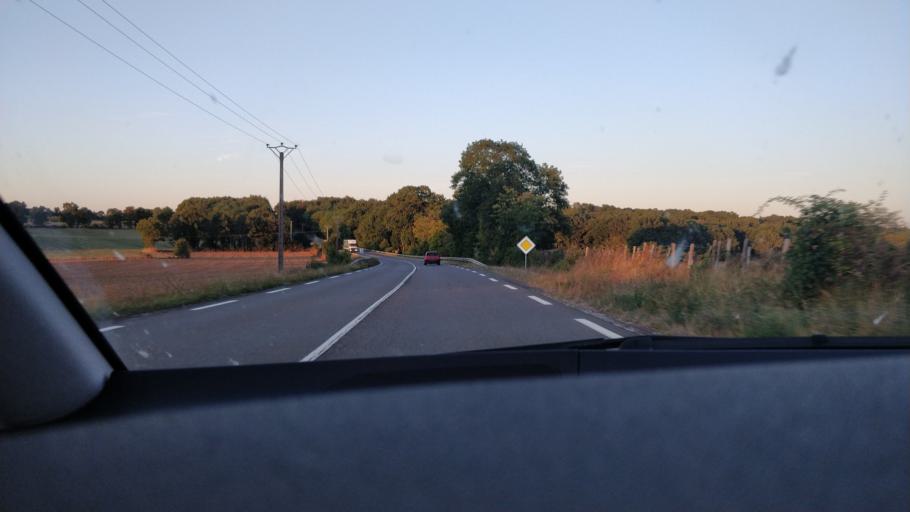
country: FR
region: Poitou-Charentes
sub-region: Departement de la Charente
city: Chasseneuil-sur-Bonnieure
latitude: 45.8389
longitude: 0.4863
